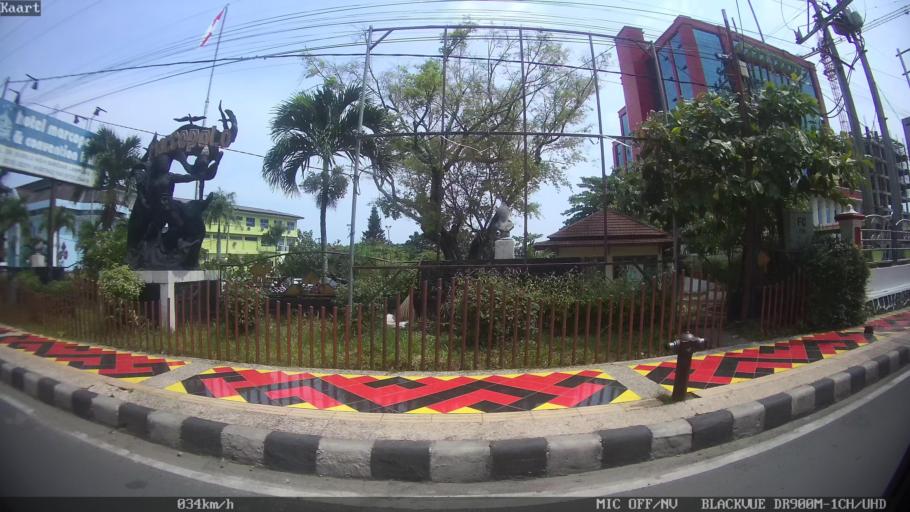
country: ID
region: Lampung
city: Bandarlampung
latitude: -5.4293
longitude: 105.2637
